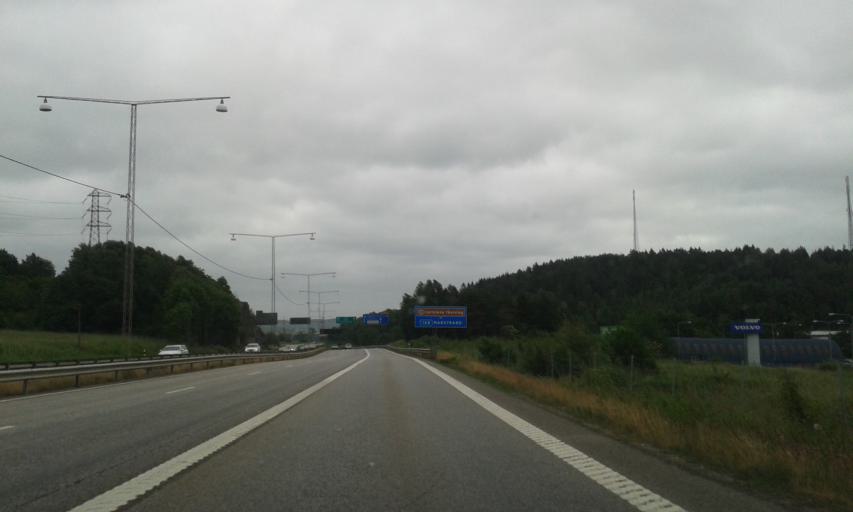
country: SE
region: Vaestra Goetaland
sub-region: Kungalvs Kommun
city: Kungalv
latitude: 57.8822
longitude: 11.9488
